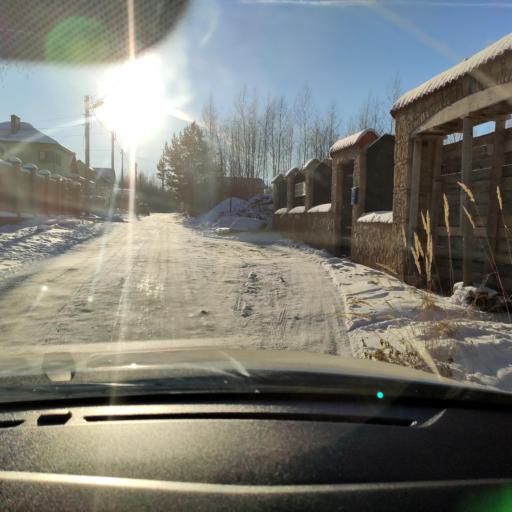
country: RU
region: Tatarstan
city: Stolbishchi
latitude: 55.7331
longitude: 49.2608
